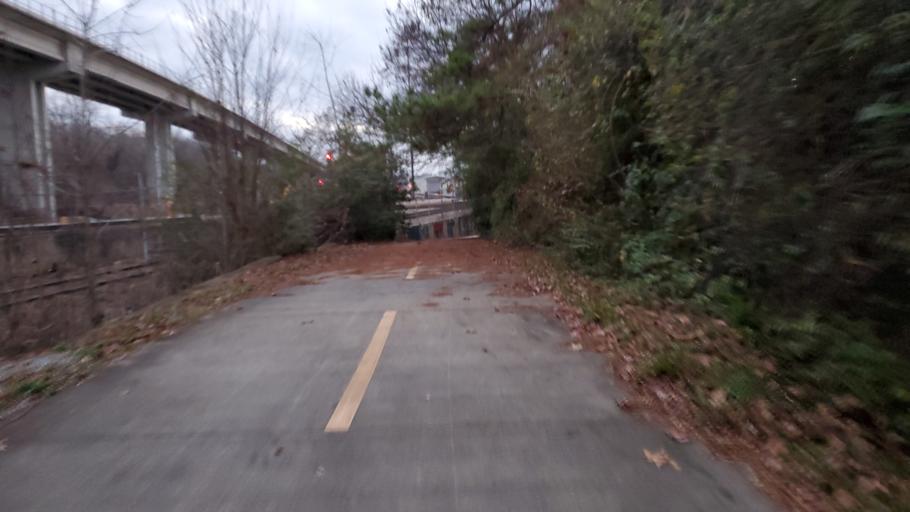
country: US
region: Georgia
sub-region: DeKalb County
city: Avondale Estates
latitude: 33.7796
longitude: -84.2695
